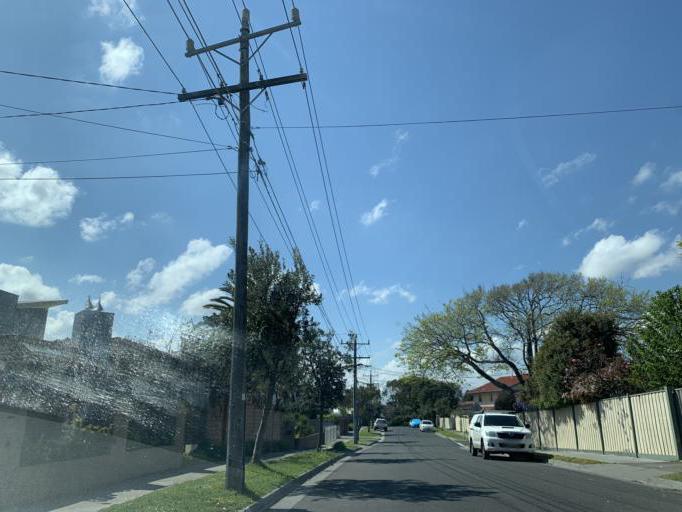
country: AU
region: Victoria
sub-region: Kingston
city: Mordialloc
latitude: -37.9982
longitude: 145.0798
